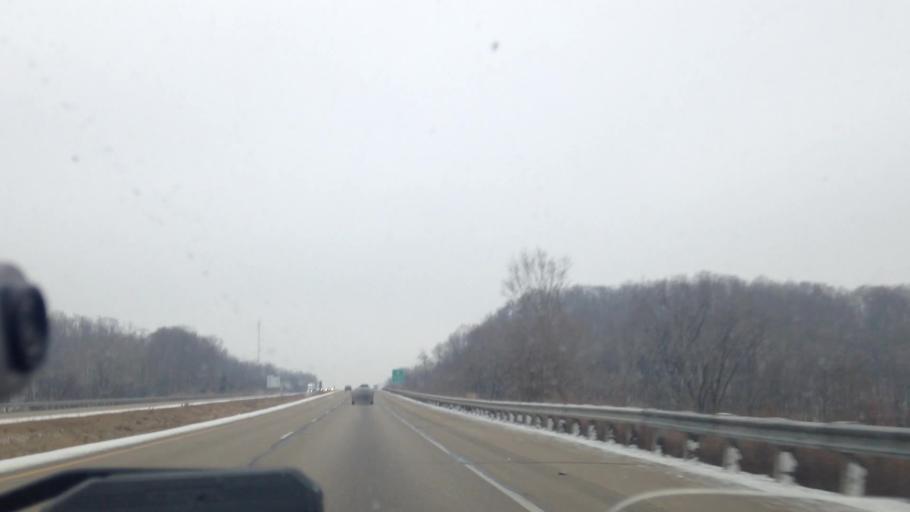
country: US
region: Wisconsin
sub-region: Washington County
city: Slinger
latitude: 43.3386
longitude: -88.2704
